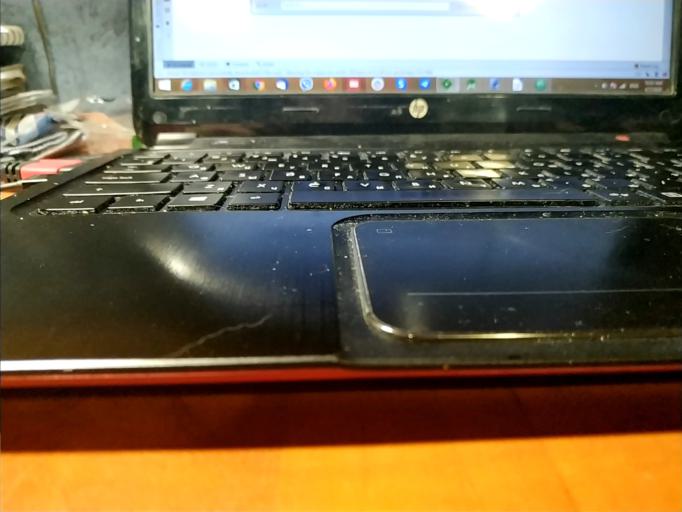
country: RU
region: Vologda
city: Suda
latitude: 58.9161
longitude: 37.5432
